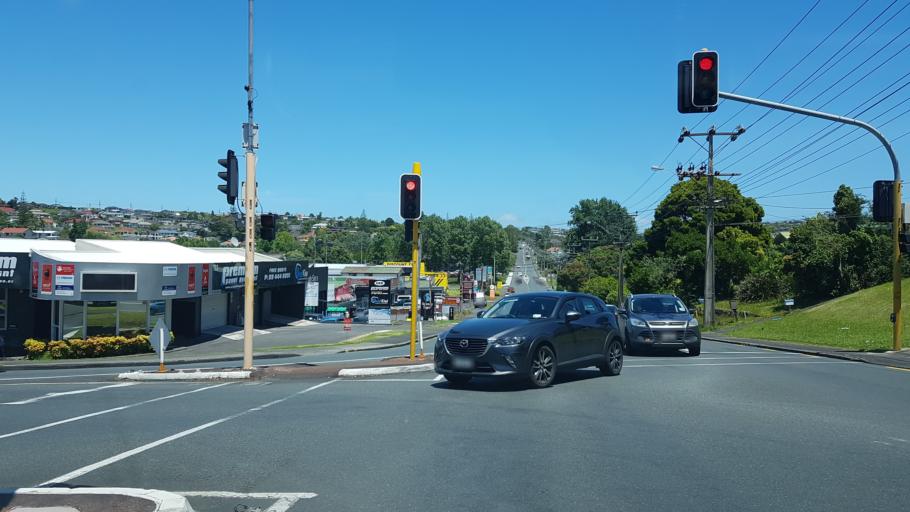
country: NZ
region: Auckland
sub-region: Auckland
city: North Shore
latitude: -36.7826
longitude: 174.7371
